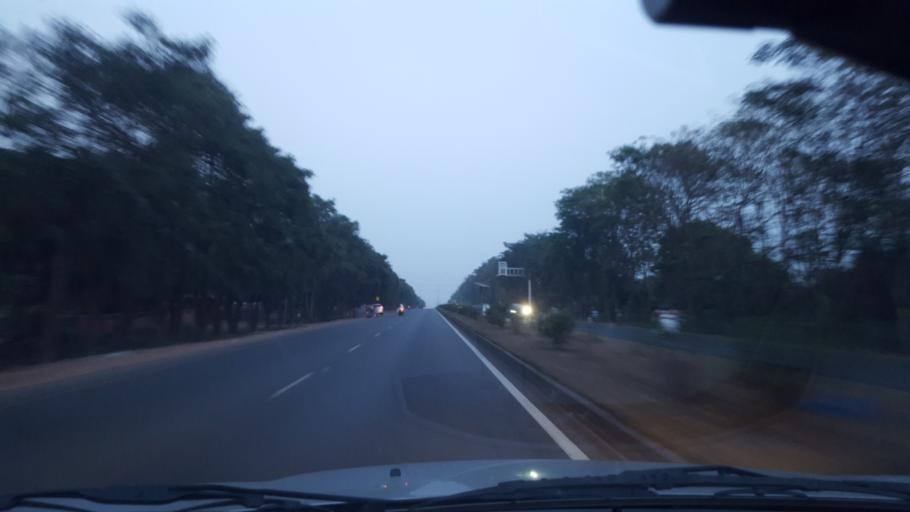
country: IN
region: Andhra Pradesh
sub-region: East Godavari
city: Rajahmundry
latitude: 17.0302
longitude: 81.8190
